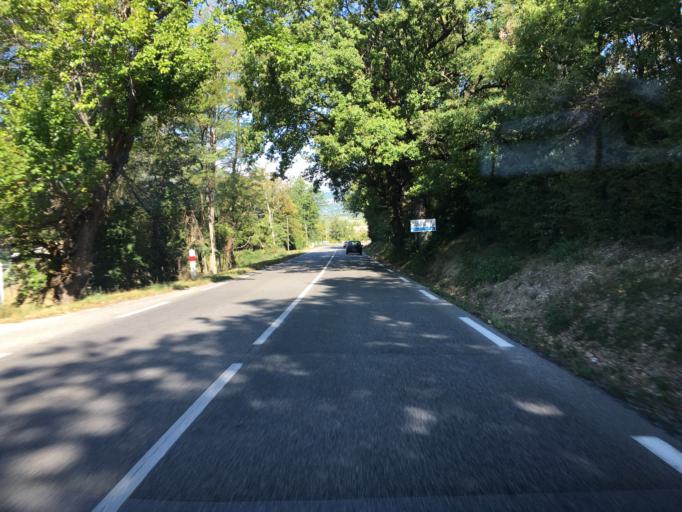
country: FR
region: Provence-Alpes-Cote d'Azur
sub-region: Departement des Hautes-Alpes
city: Laragne-Monteglin
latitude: 44.2883
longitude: 5.8436
